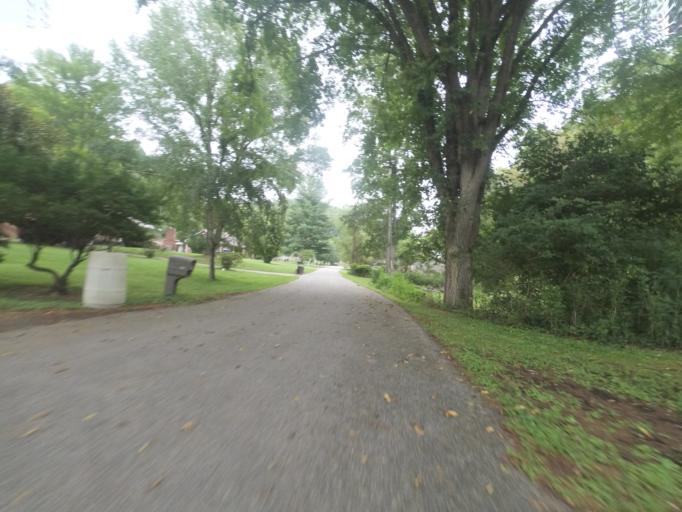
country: US
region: West Virginia
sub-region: Cabell County
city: Huntington
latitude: 38.3954
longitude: -82.4489
